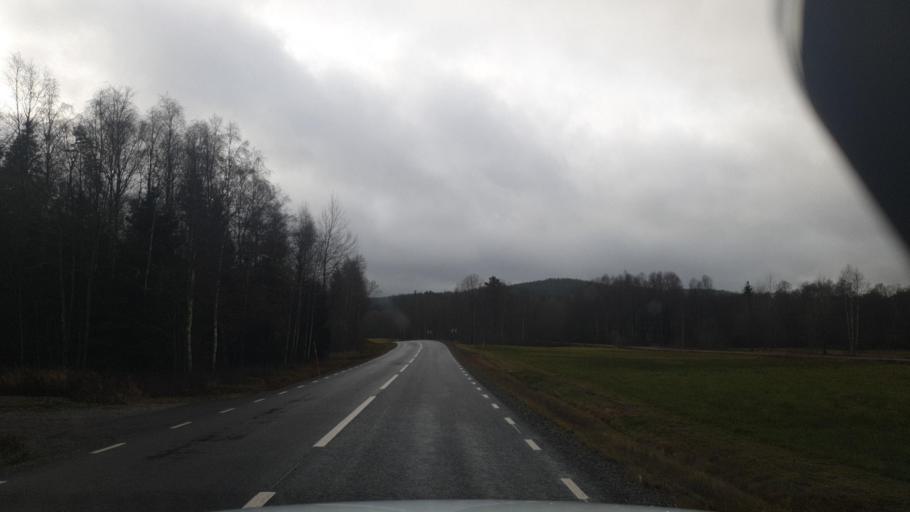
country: SE
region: Vaermland
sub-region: Arjangs Kommun
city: Arjaeng
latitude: 59.5835
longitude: 12.1247
